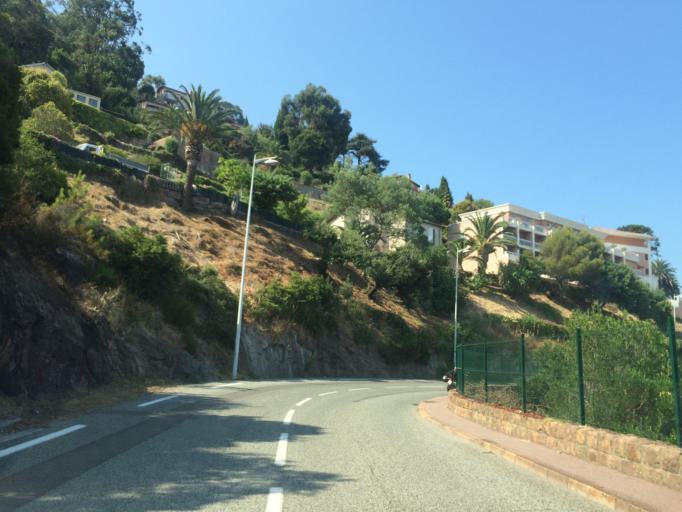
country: FR
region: Provence-Alpes-Cote d'Azur
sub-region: Departement des Alpes-Maritimes
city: Theoule-sur-Mer
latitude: 43.4994
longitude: 6.9513
